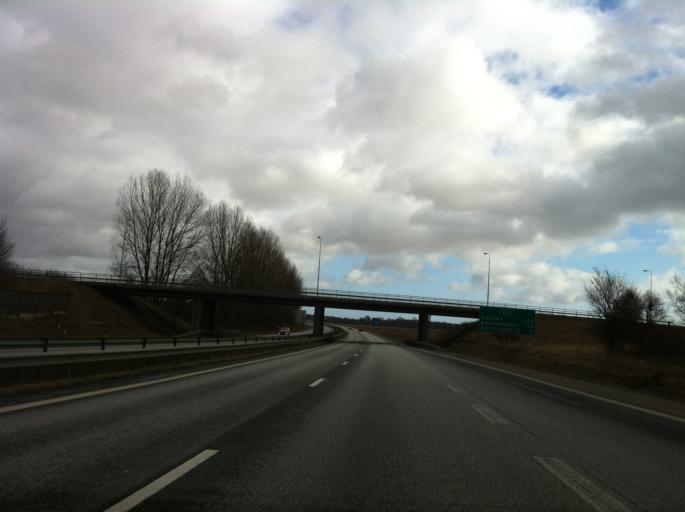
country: SE
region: Skane
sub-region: Kristianstads Kommun
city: Kristianstad
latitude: 56.0196
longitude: 14.1111
